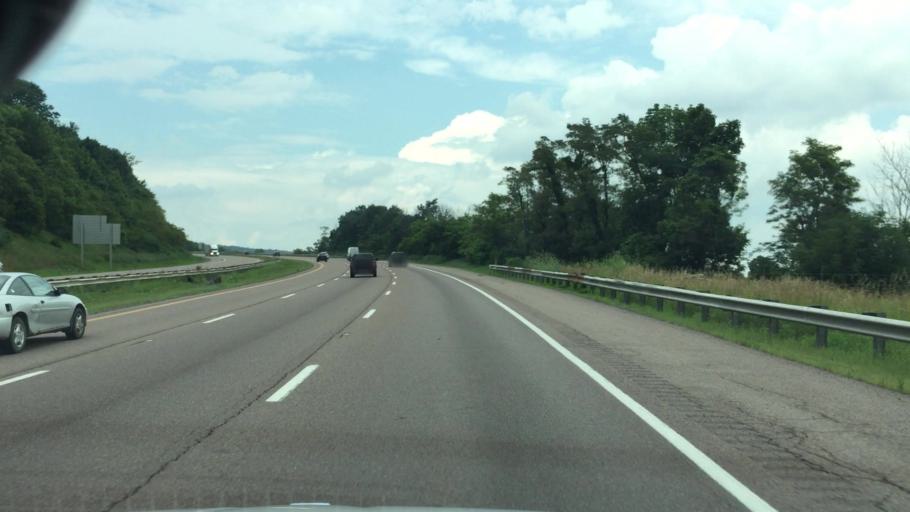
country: US
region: Maryland
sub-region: Allegany County
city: Frostburg
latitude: 39.6539
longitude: -78.9538
